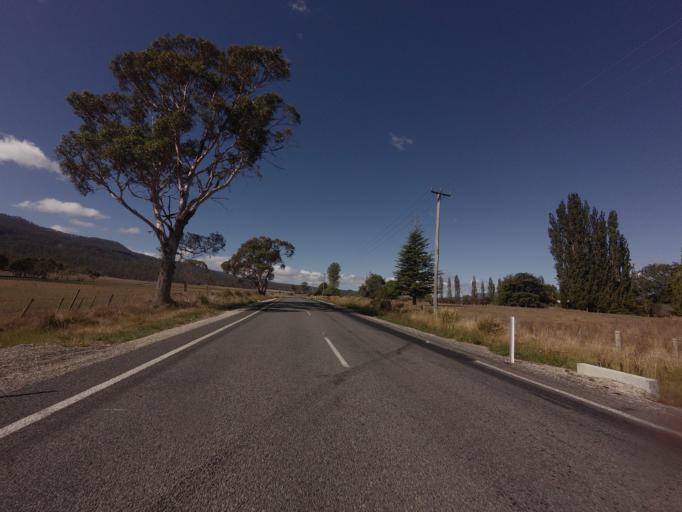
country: AU
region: Tasmania
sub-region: Break O'Day
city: St Helens
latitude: -41.5777
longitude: 148.1066
